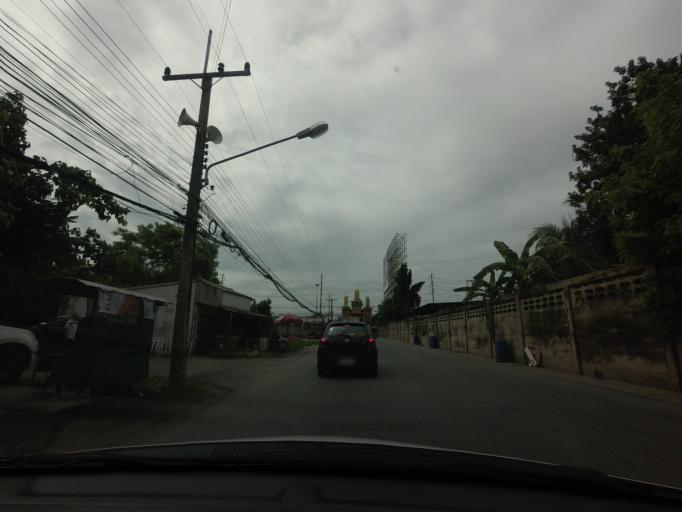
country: TH
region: Pathum Thani
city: Lam Luk Ka
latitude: 13.9327
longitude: 100.7132
